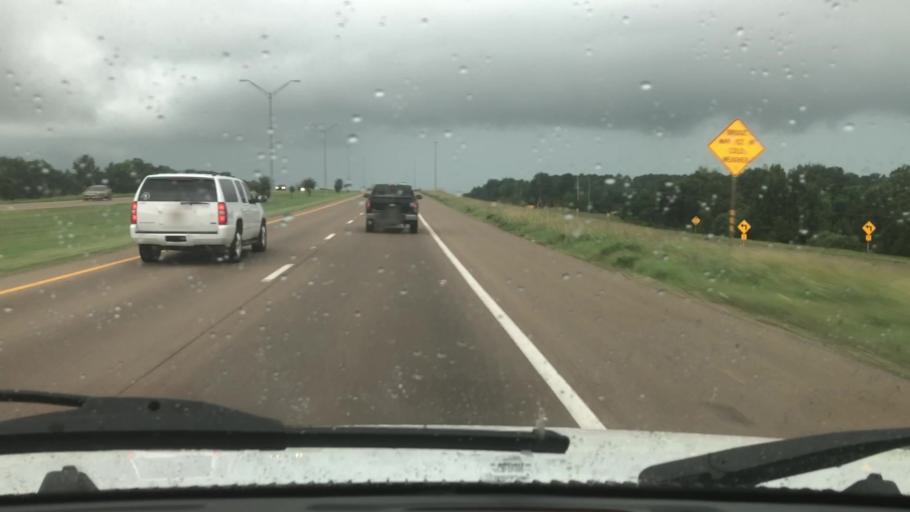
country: US
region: Texas
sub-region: Bowie County
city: Wake Village
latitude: 33.4053
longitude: -94.0978
